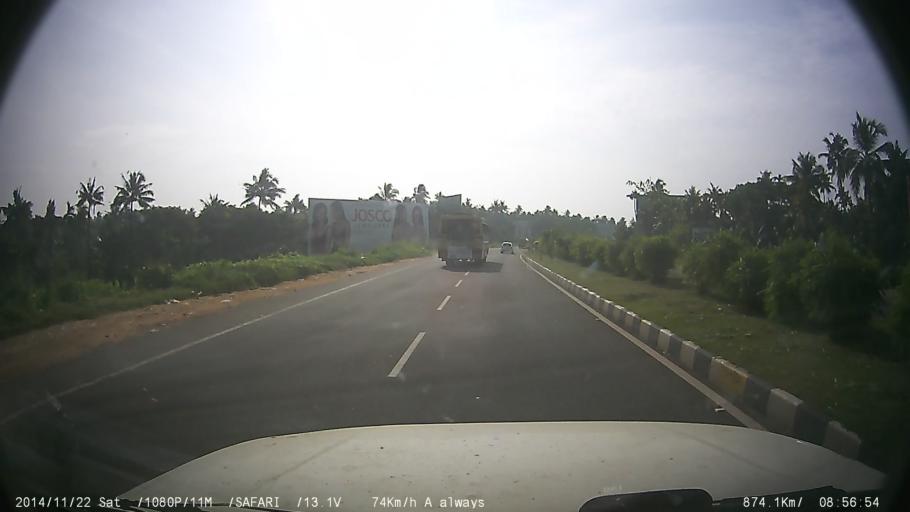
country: IN
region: Kerala
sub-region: Thrissur District
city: Irinjalakuda
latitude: 10.4115
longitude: 76.2723
